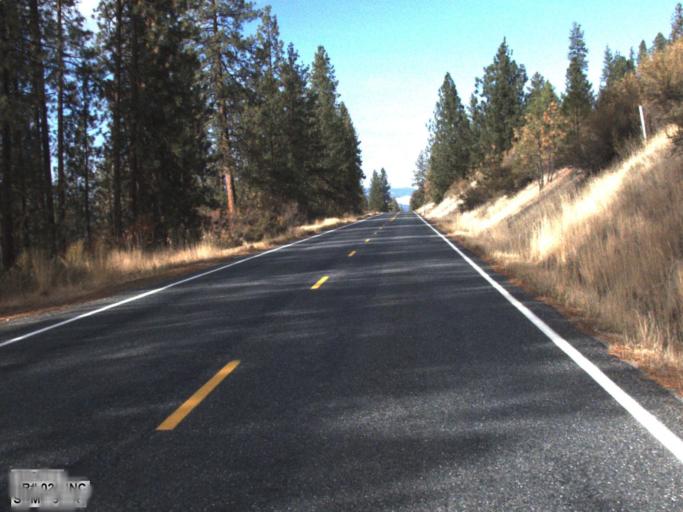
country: US
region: Washington
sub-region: Stevens County
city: Kettle Falls
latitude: 48.3186
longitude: -118.1496
